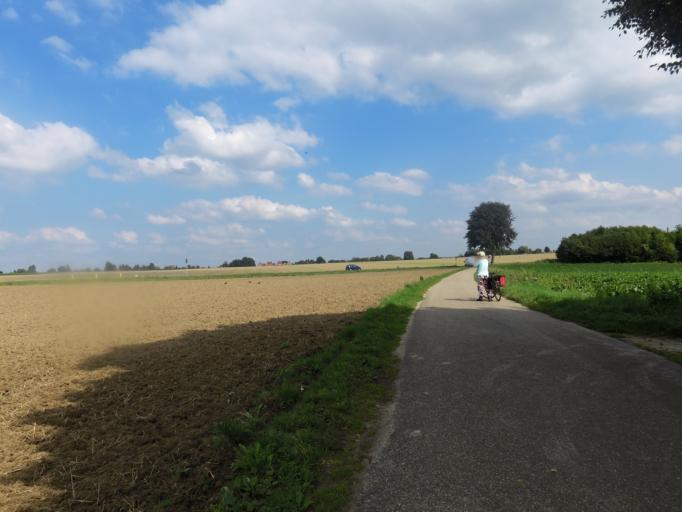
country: NL
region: Limburg
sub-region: Gemeente Schinnen
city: Puth
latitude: 50.9514
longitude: 5.8610
